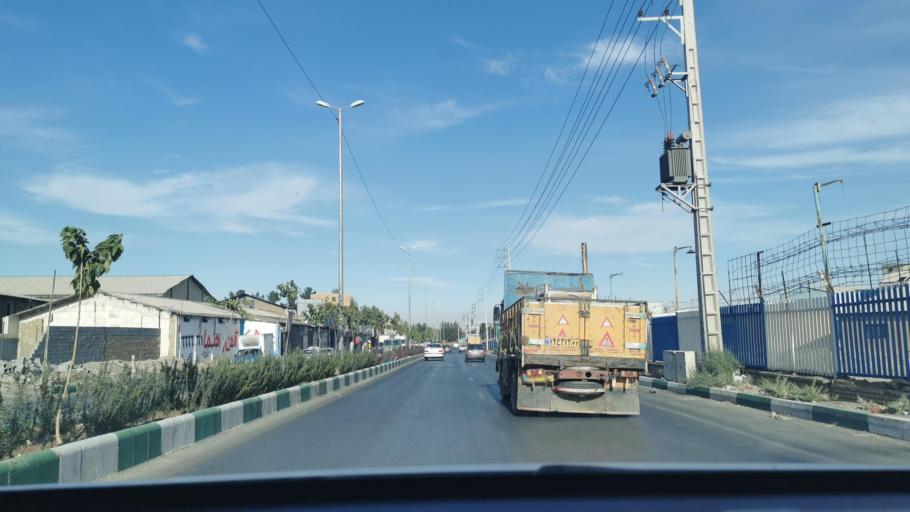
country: IR
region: Razavi Khorasan
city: Torqabeh
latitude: 36.4374
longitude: 59.4388
